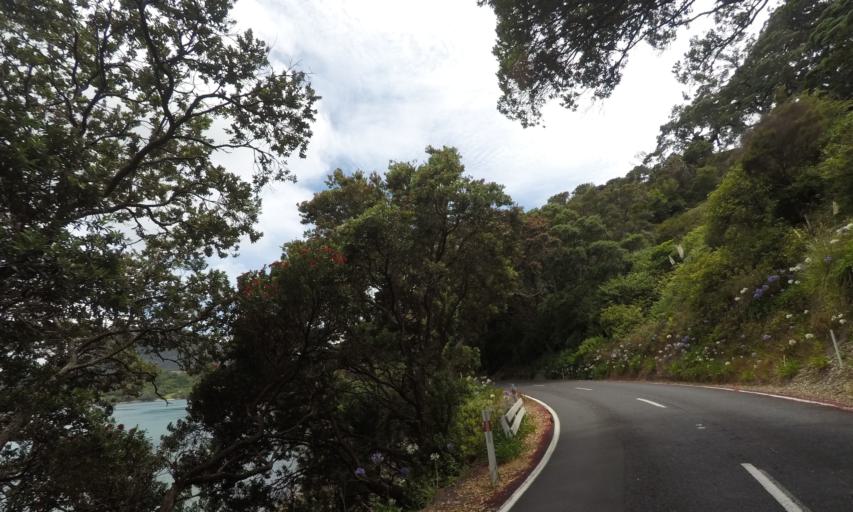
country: NZ
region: Northland
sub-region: Whangarei
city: Ruakaka
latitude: -35.8388
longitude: 174.5339
